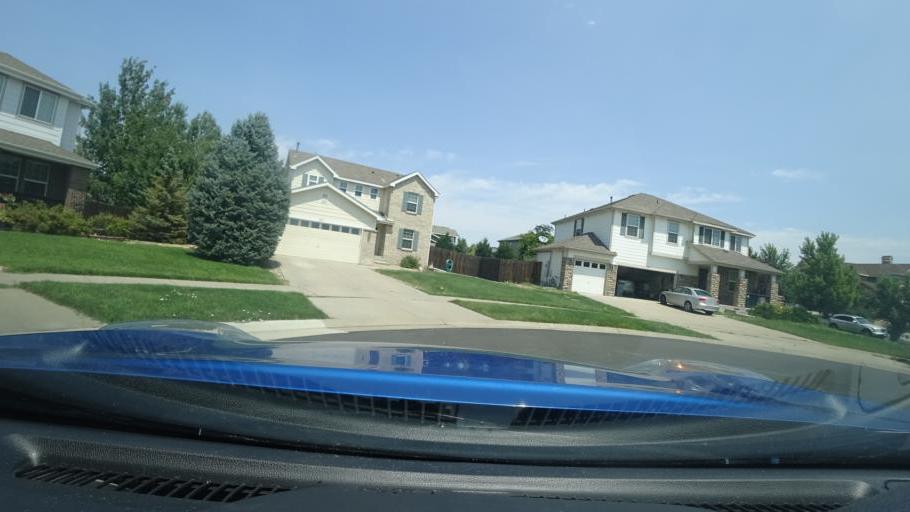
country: US
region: Colorado
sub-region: Adams County
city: Aurora
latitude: 39.6737
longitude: -104.7592
